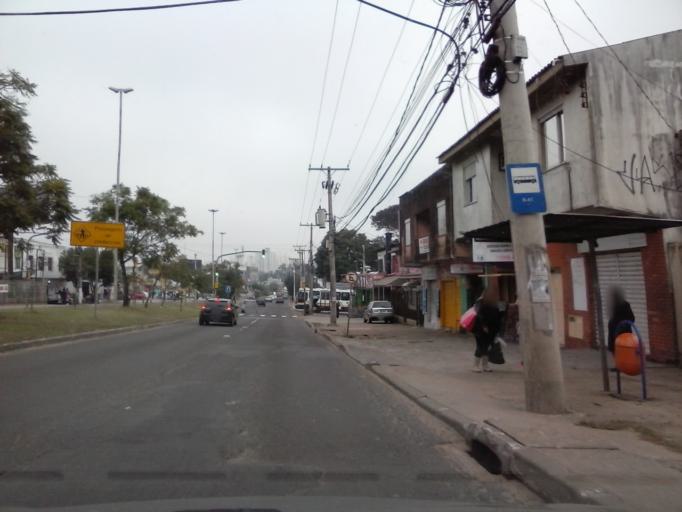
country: BR
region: Rio Grande do Sul
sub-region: Cachoeirinha
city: Cachoeirinha
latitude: -30.0390
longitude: -51.1233
